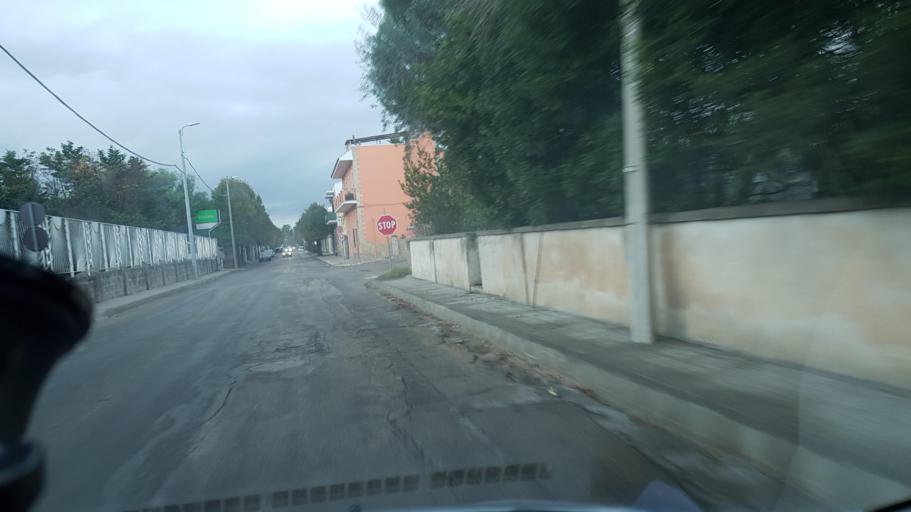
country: IT
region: Apulia
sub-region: Provincia di Lecce
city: Novoli
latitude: 40.3648
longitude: 18.0732
